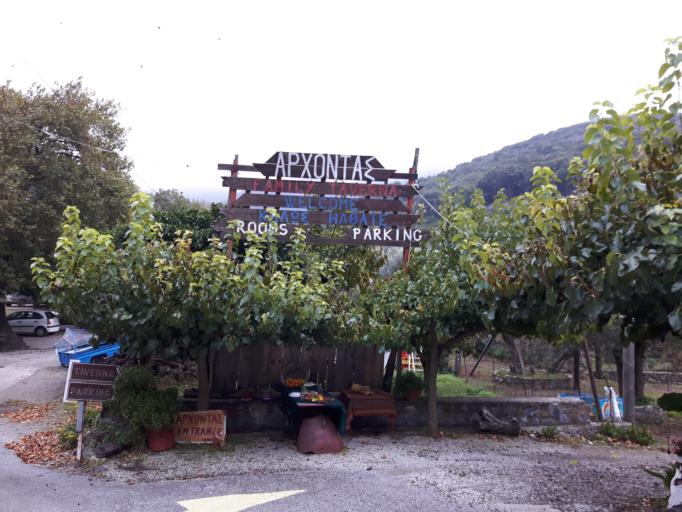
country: GR
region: Crete
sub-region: Nomos Chanias
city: Kissamos
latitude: 35.4055
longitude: 23.6827
